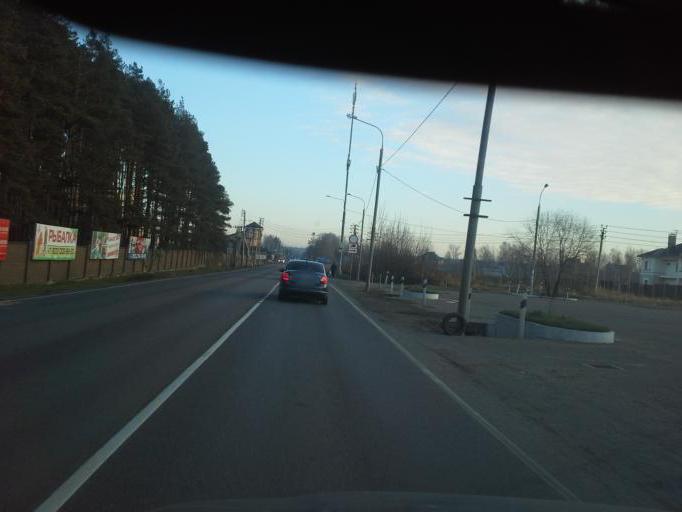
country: RU
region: Moskovskaya
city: Kokoshkino
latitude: 55.5797
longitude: 37.1277
